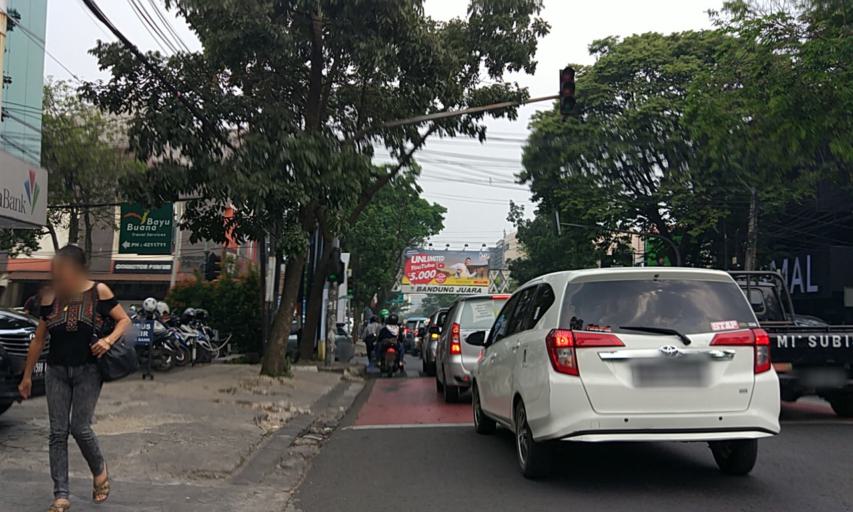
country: ID
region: West Java
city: Bandung
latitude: -6.9037
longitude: 107.5976
